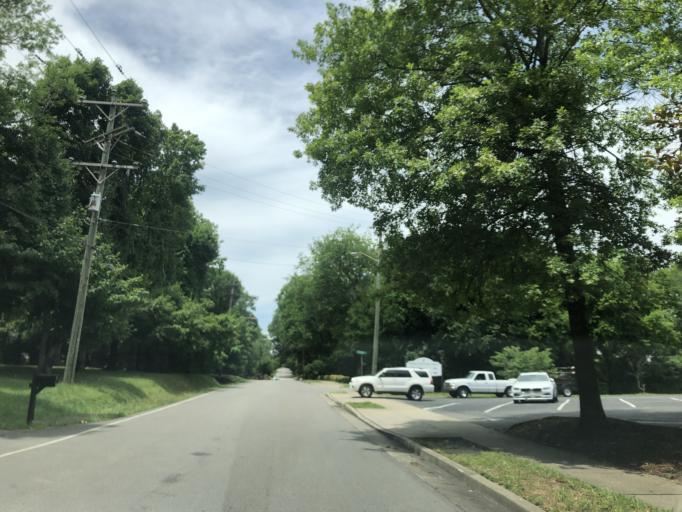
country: US
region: Tennessee
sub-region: Davidson County
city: Oak Hill
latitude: 36.1104
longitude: -86.8014
